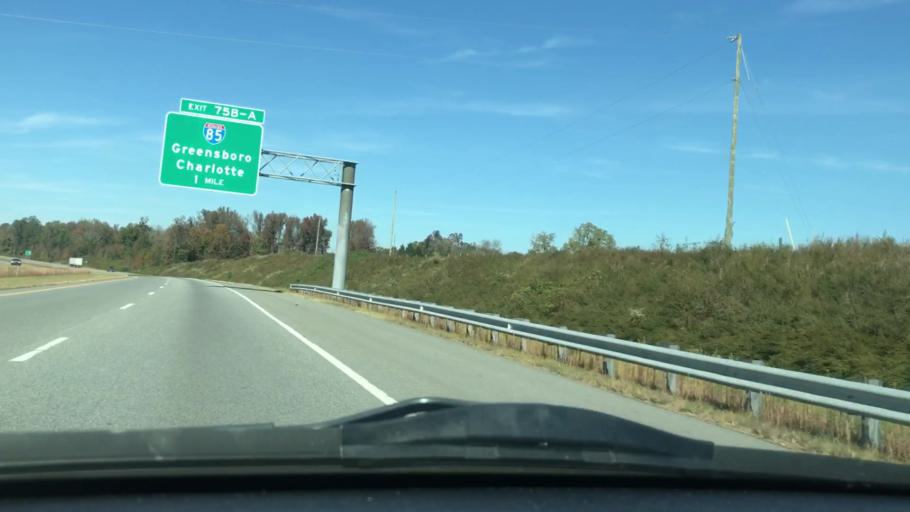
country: US
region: North Carolina
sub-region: Randolph County
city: Archdale
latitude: 35.9113
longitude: -79.9129
